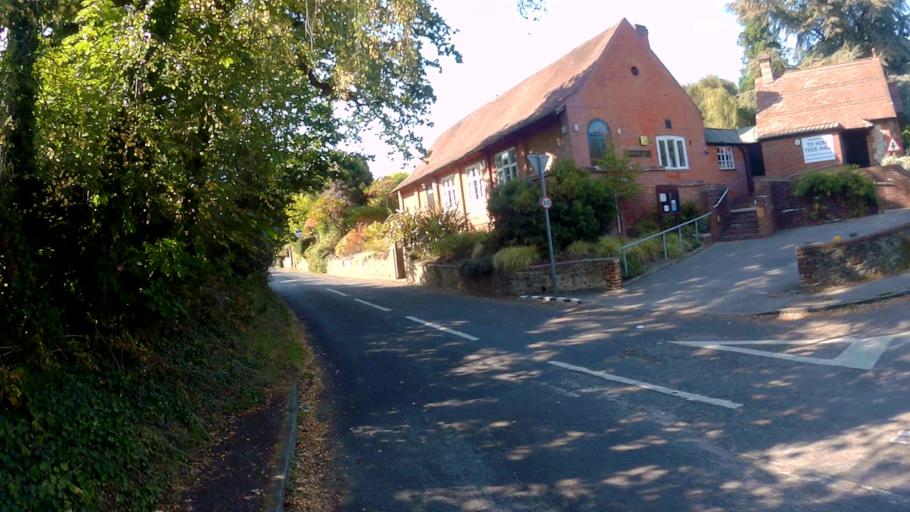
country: GB
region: England
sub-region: Surrey
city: Churt
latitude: 51.1731
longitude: -0.7881
